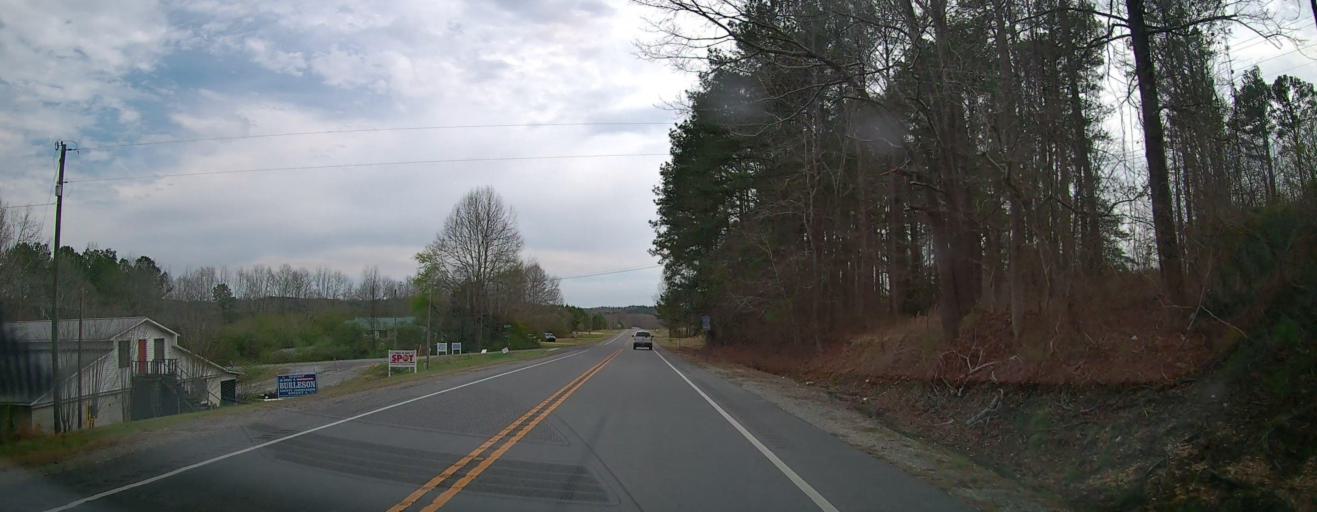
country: US
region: Alabama
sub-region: Marion County
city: Guin
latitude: 34.0101
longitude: -87.9349
